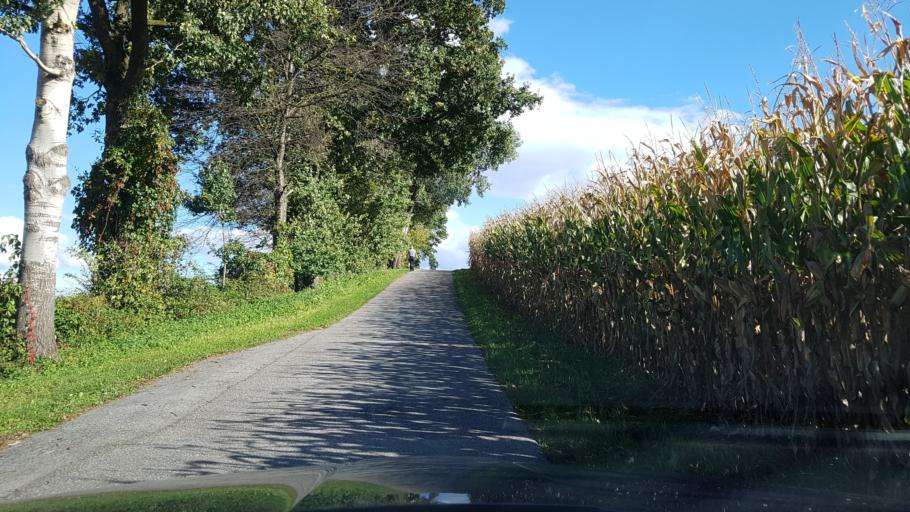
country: AT
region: Styria
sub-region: Politischer Bezirk Deutschlandsberg
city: Sankt Martin im Sulmtal
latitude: 46.7471
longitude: 15.2882
